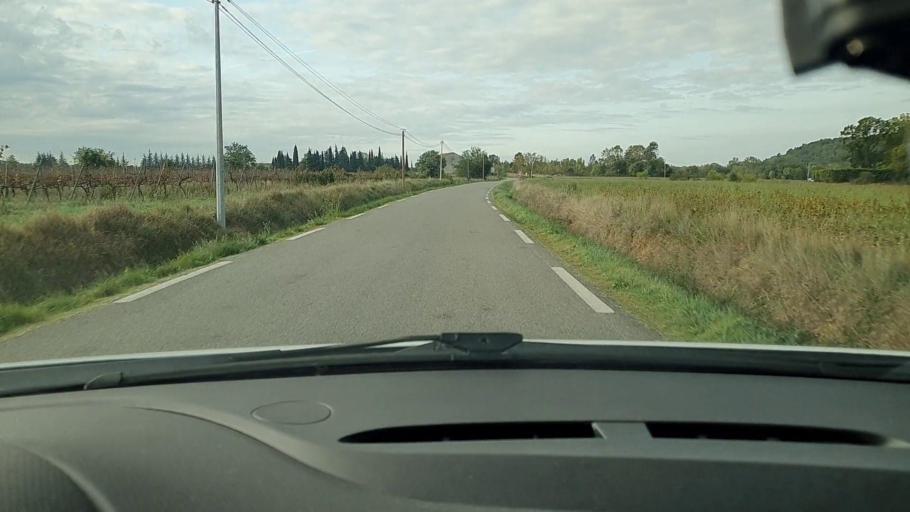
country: FR
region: Languedoc-Roussillon
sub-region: Departement du Gard
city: Les Mages
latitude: 44.1886
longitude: 4.2367
